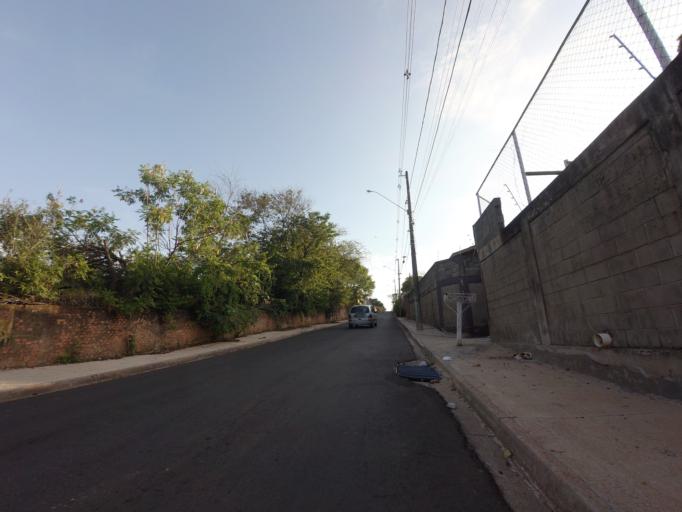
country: BR
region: Sao Paulo
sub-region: Piracicaba
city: Piracicaba
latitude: -22.7479
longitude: -47.6087
